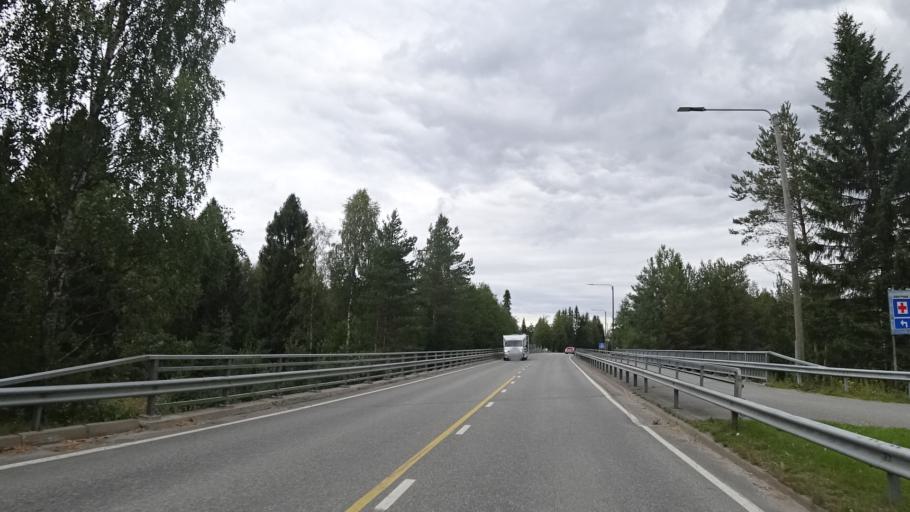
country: FI
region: North Karelia
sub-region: Joensuu
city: Ilomantsi
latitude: 62.6642
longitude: 30.9361
